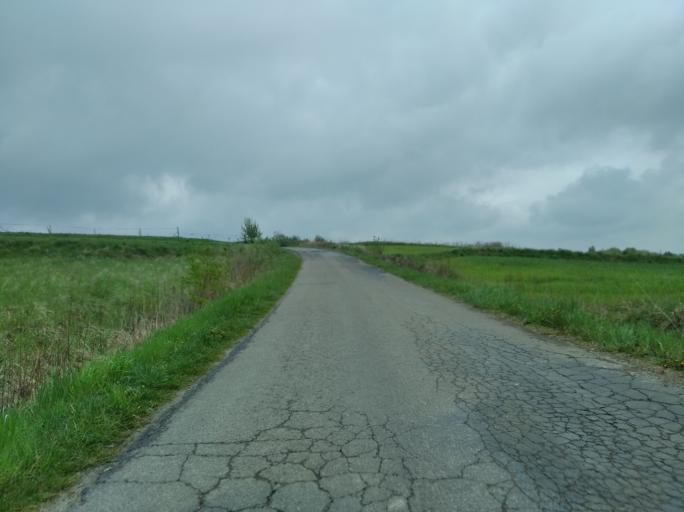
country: PL
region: Subcarpathian Voivodeship
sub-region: Powiat brzozowski
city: Golcowa
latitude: 49.7520
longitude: 22.0467
